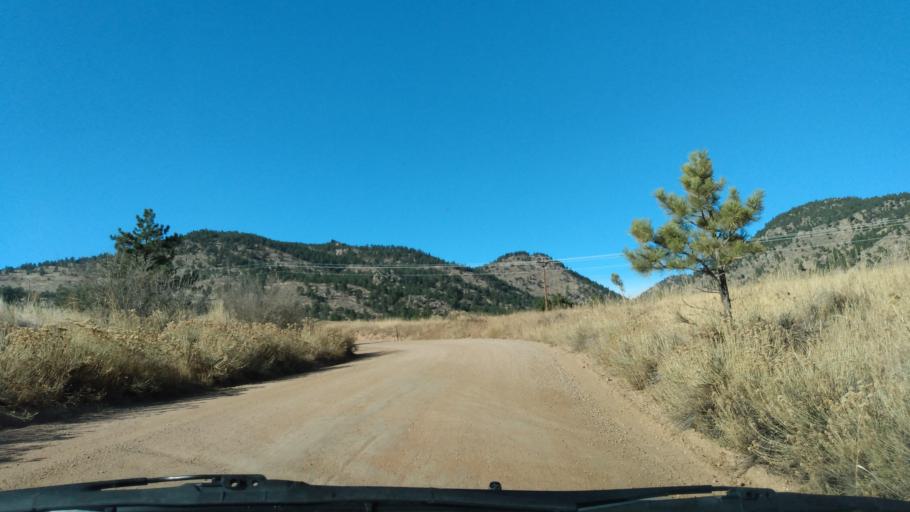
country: US
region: Colorado
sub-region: Boulder County
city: Lyons
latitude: 40.2341
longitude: -105.3247
